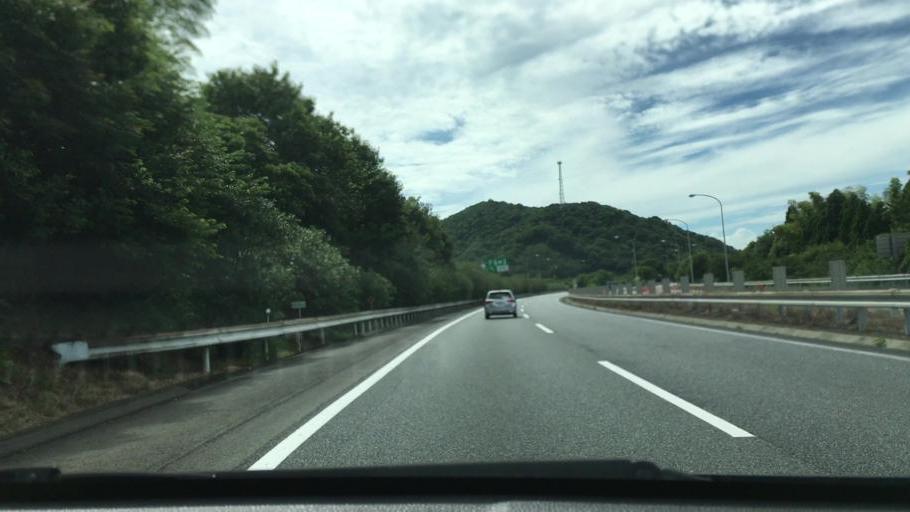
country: JP
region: Yamaguchi
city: Hofu
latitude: 34.0512
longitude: 131.5140
